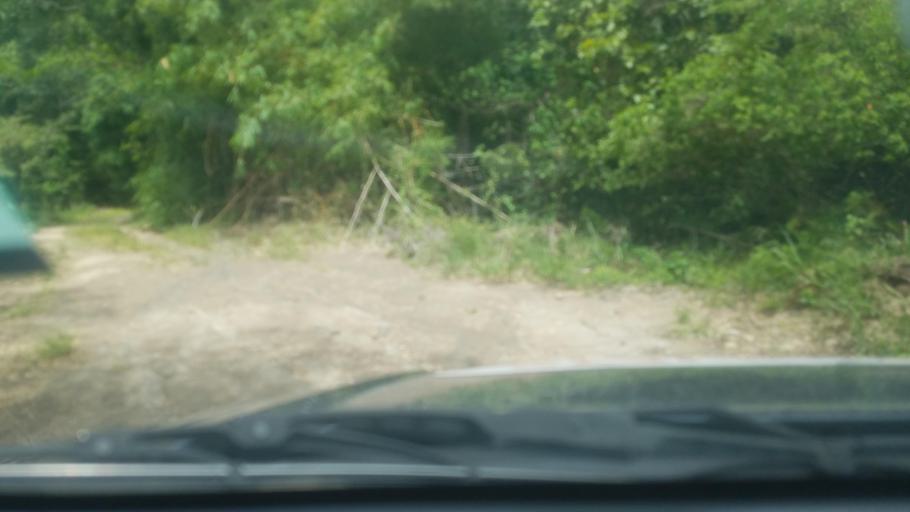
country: LC
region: Laborie Quarter
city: Laborie
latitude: 13.7578
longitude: -60.9848
